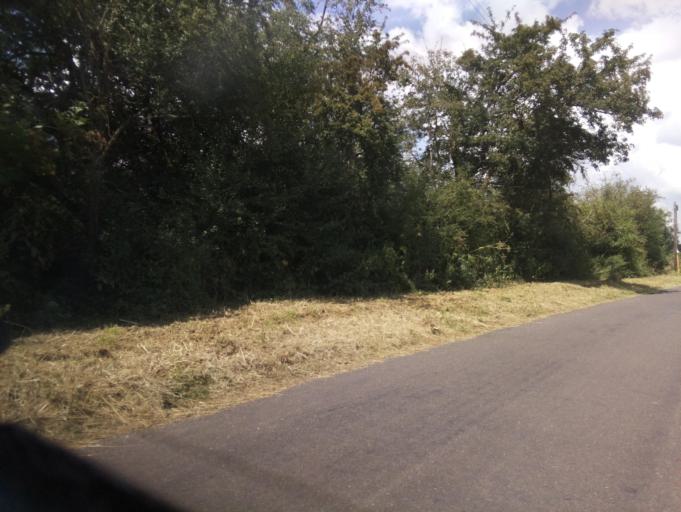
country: GB
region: England
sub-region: Wiltshire
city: Hankerton
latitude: 51.6256
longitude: -2.0263
